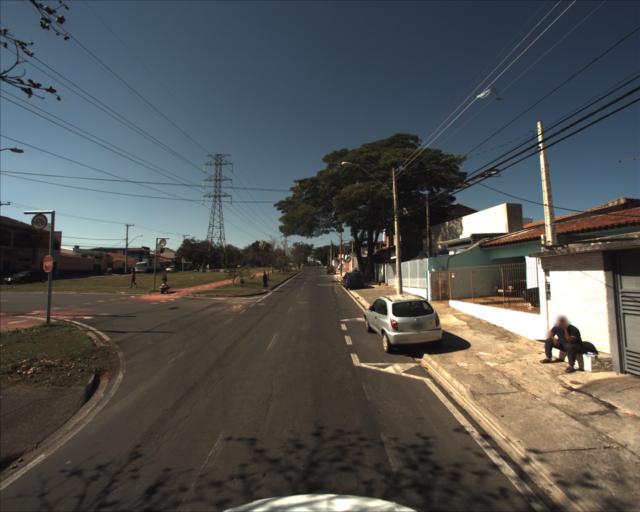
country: BR
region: Sao Paulo
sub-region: Sorocaba
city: Sorocaba
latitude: -23.5064
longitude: -47.5054
